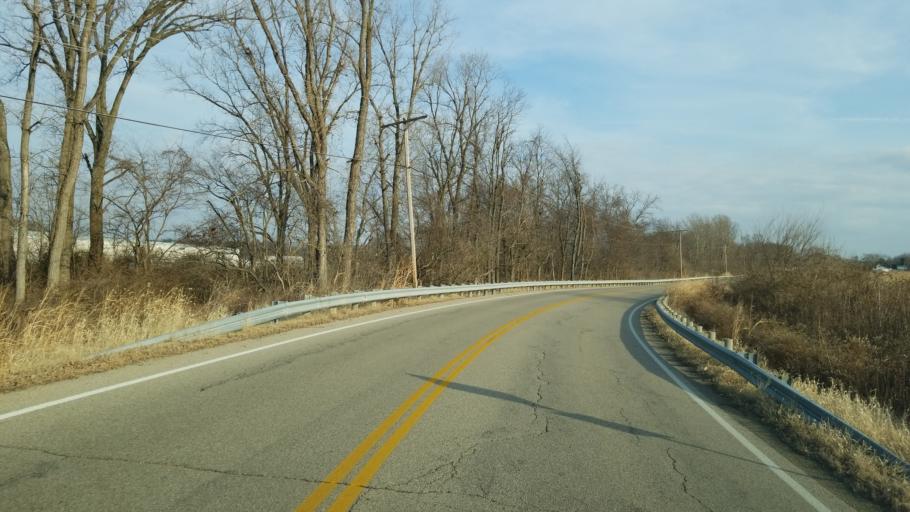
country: US
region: Ohio
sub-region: Ross County
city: Chillicothe
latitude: 39.3869
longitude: -82.9629
